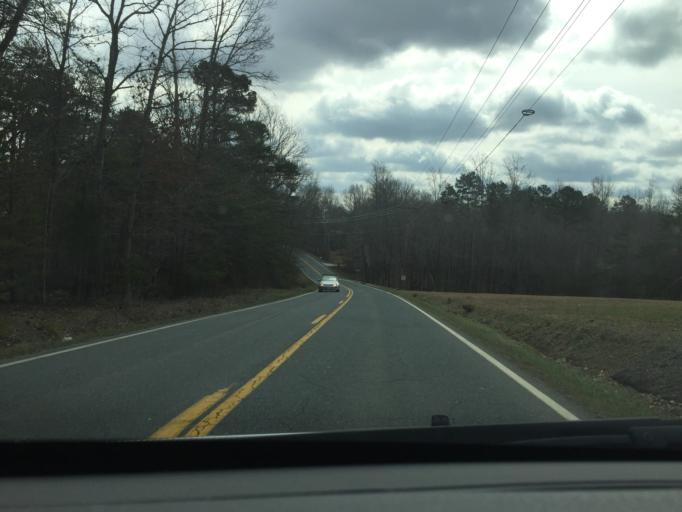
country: US
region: Virginia
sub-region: City of Lynchburg
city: West Lynchburg
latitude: 37.3315
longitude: -79.1675
